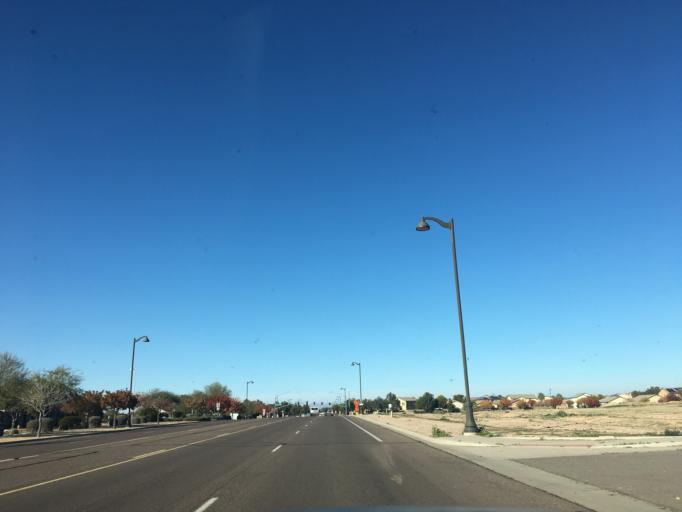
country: US
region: Arizona
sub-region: Pinal County
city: Maricopa
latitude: 33.0413
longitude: -112.0128
